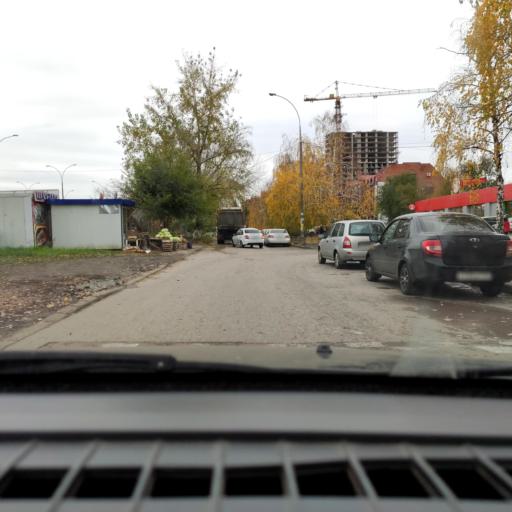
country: RU
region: Samara
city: Tol'yatti
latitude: 53.5277
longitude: 49.2910
